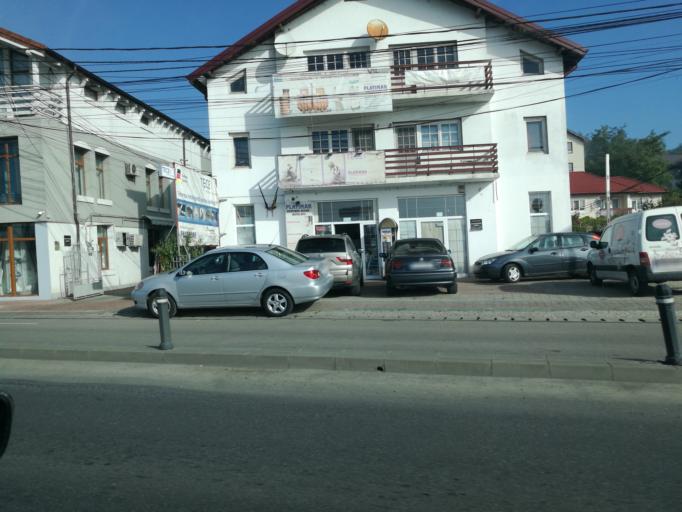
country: RO
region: Iasi
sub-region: Comuna Valea Lupului
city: Valea Lupului
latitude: 47.1729
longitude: 27.5135
